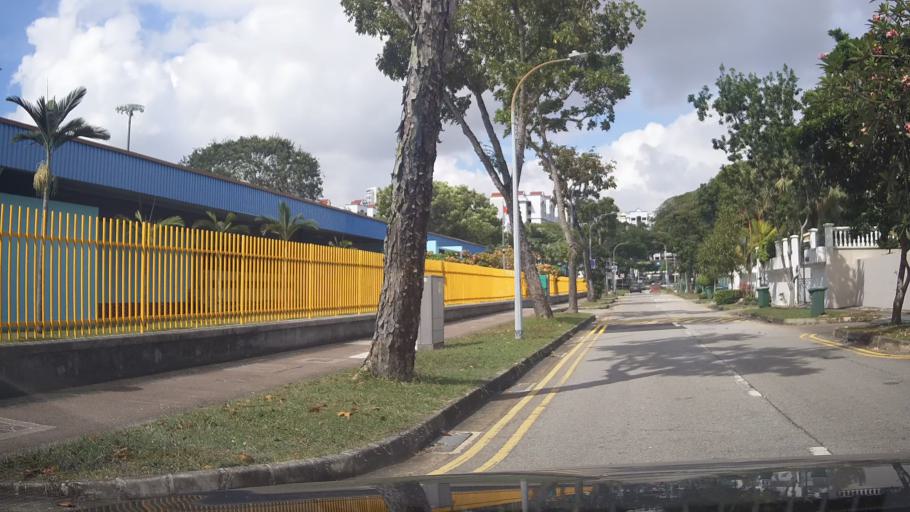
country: SG
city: Singapore
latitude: 1.3022
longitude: 103.8865
